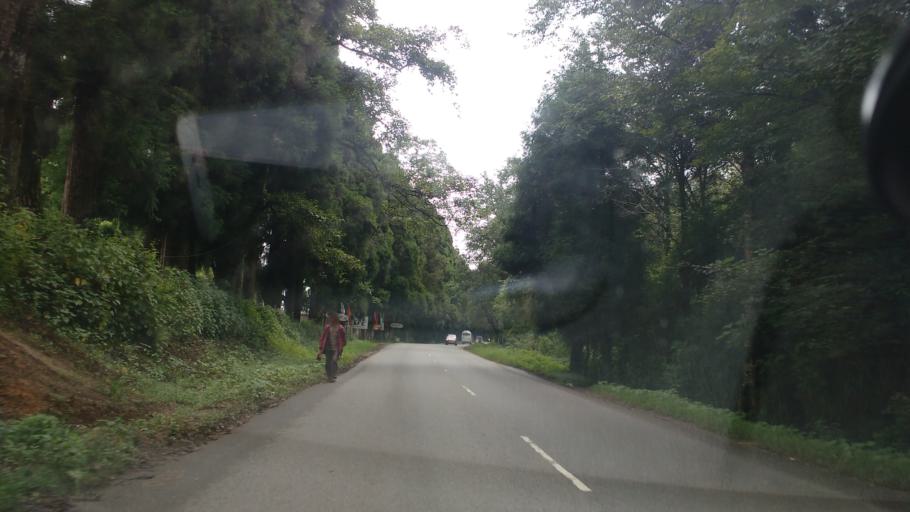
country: IN
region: Meghalaya
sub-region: East Khasi Hills
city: Shillong
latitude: 25.5469
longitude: 91.8389
